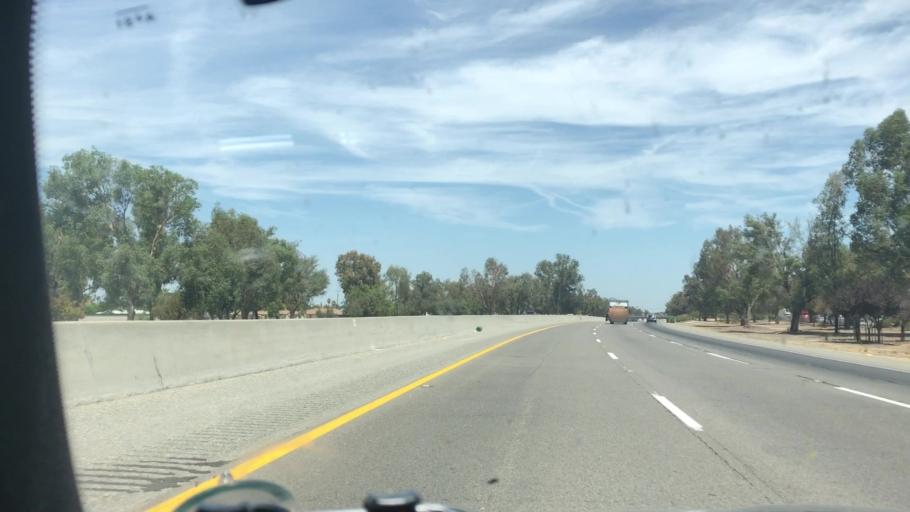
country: US
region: California
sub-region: Kern County
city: Delano
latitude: 35.7562
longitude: -119.2477
